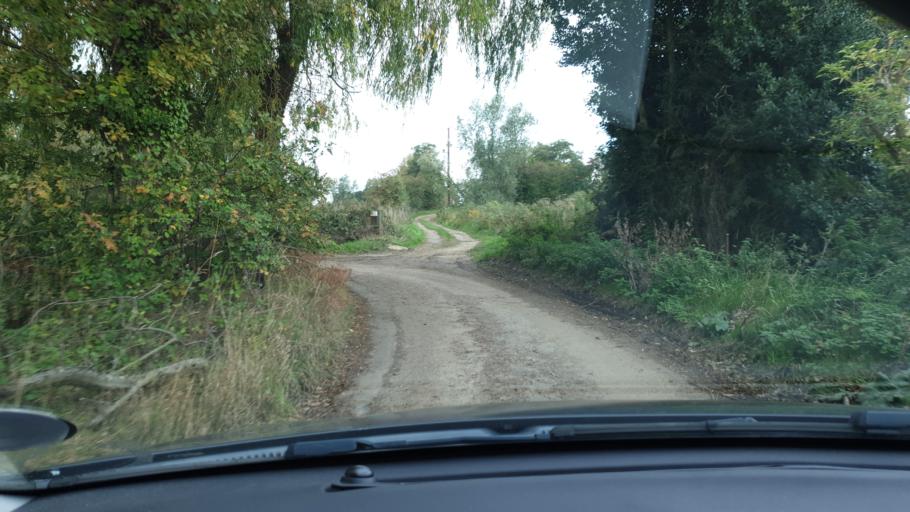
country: GB
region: England
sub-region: Essex
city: Mistley
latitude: 51.9318
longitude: 1.1067
